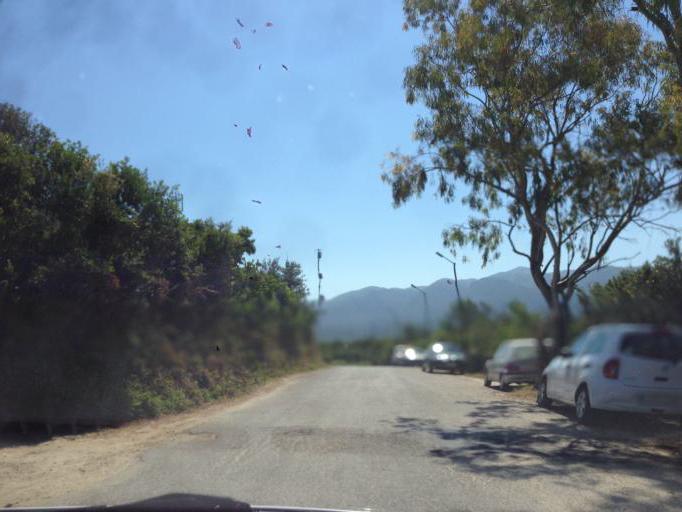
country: GR
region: Ionian Islands
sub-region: Nomos Kerkyras
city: Acharavi
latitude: 39.7930
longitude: 19.7783
